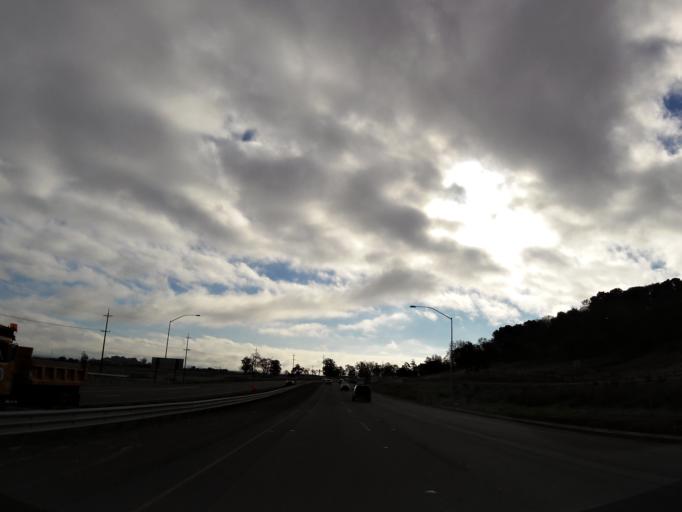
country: US
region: California
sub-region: Marin County
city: Novato
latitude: 38.1613
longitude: -122.5732
